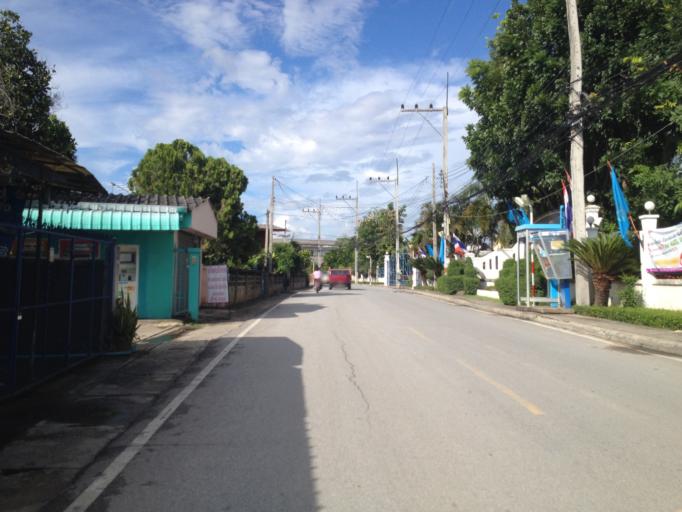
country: TH
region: Chiang Mai
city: Hang Dong
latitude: 18.6885
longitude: 98.9187
